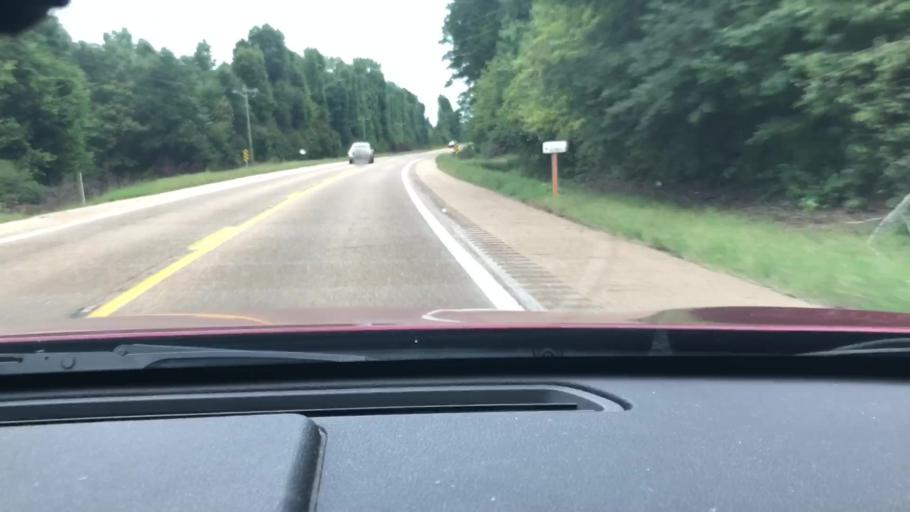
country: US
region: Arkansas
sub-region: Miller County
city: Texarkana
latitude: 33.4191
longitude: -93.8373
